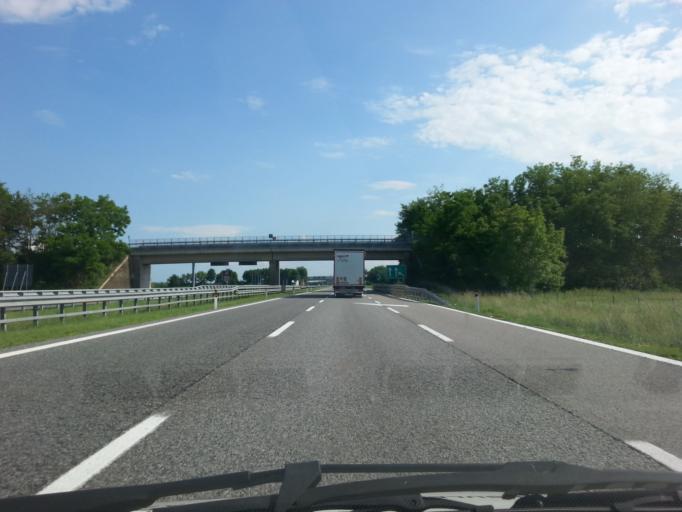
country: IT
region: Piedmont
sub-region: Provincia di Torino
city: Carmagnola
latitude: 44.8487
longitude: 7.7488
